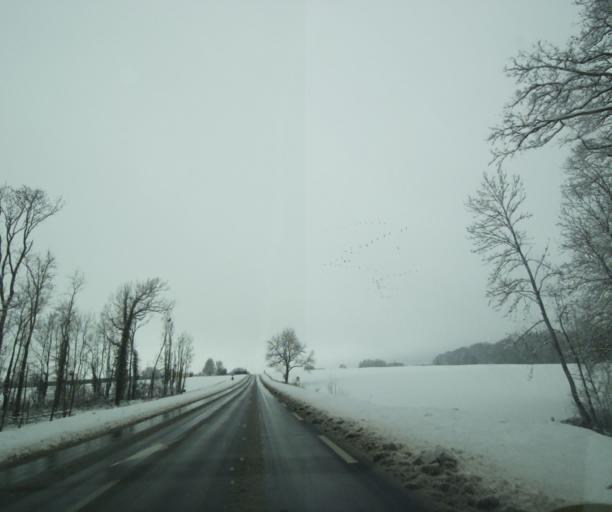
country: FR
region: Champagne-Ardenne
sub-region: Departement de la Haute-Marne
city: Montier-en-Der
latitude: 48.5401
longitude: 4.8235
